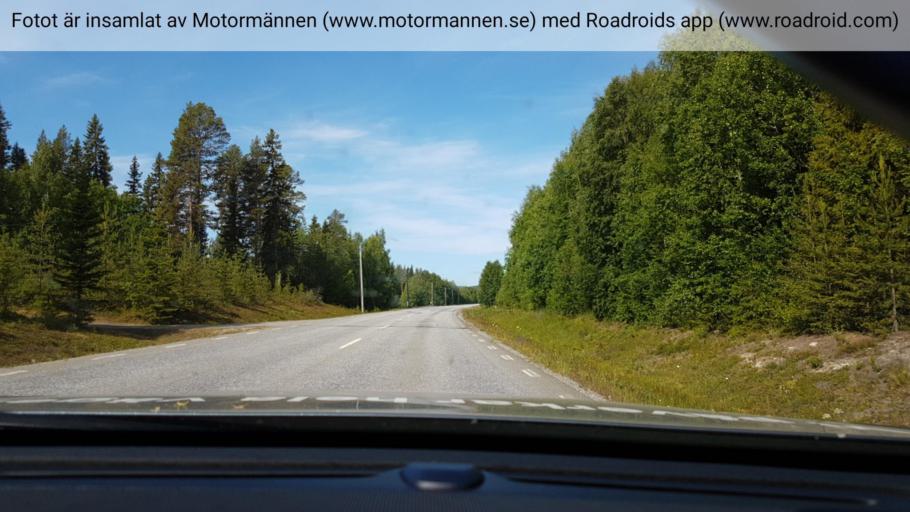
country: SE
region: Vaesterbotten
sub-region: Dorotea Kommun
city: Dorotea
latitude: 64.2487
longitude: 16.5248
